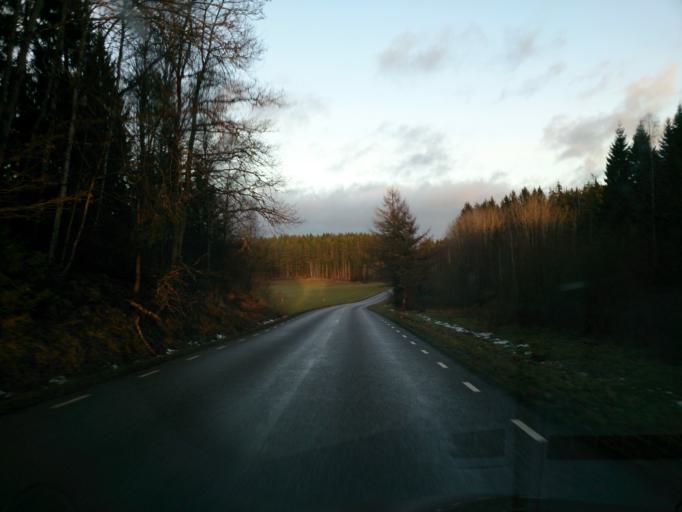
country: SE
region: OEstergoetland
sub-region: Atvidabergs Kommun
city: Atvidaberg
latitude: 58.2987
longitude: 16.0096
